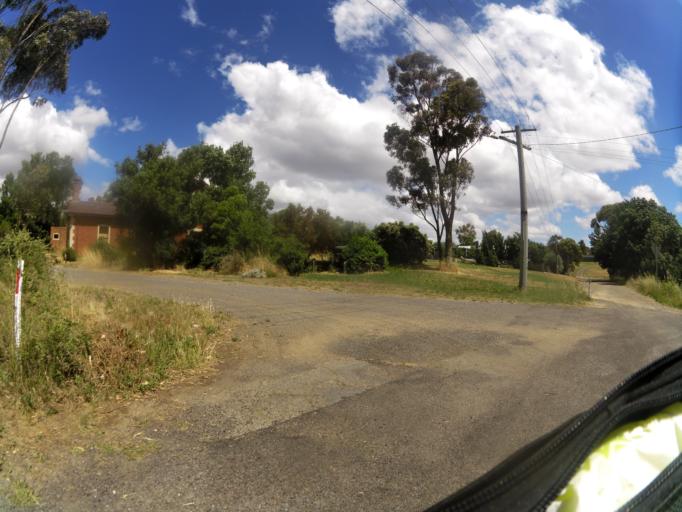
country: AU
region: Victoria
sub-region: Mount Alexander
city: Castlemaine
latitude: -37.0037
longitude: 144.2529
